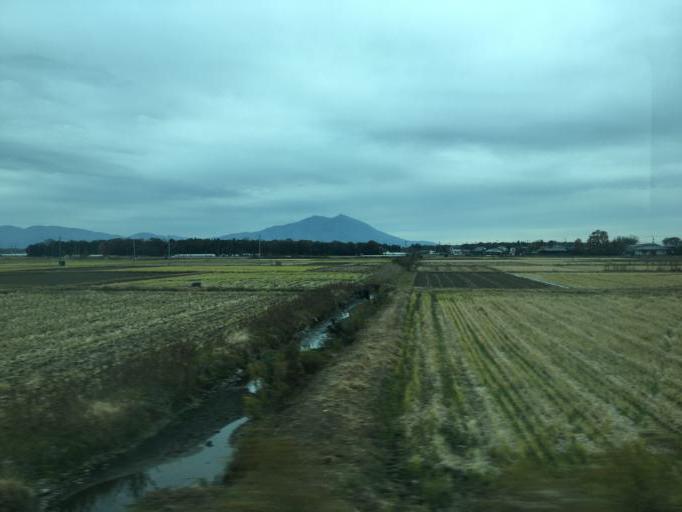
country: JP
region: Ibaraki
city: Shimodate
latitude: 36.3202
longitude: 140.0244
